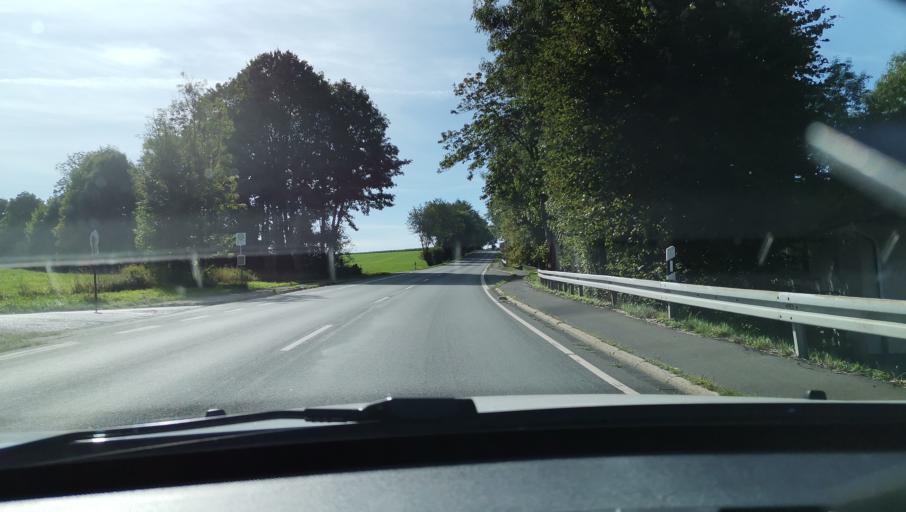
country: DE
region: North Rhine-Westphalia
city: Halver
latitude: 51.2228
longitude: 7.4846
